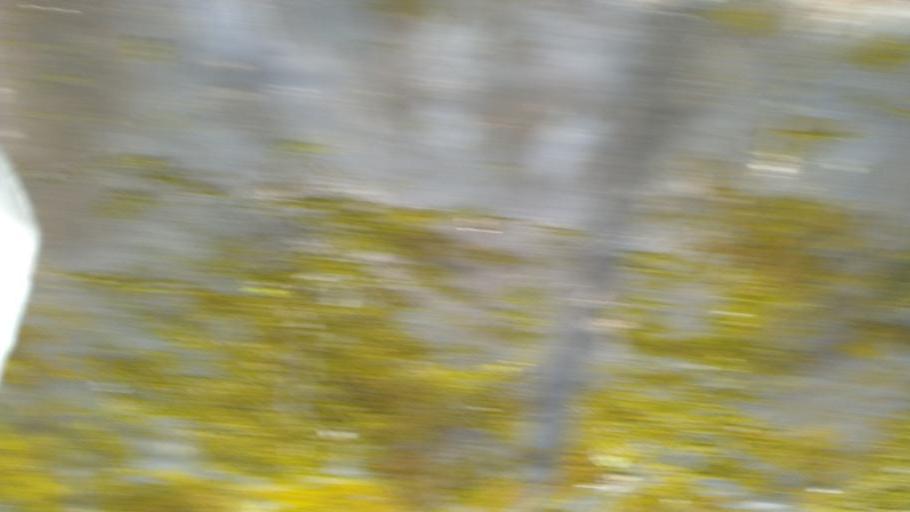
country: JP
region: Kyoto
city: Ayabe
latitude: 35.3304
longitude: 135.3514
